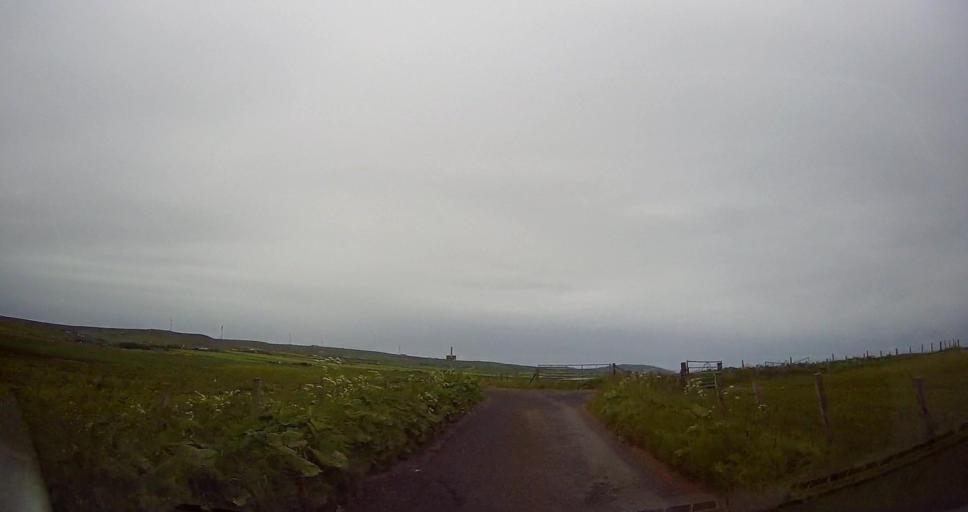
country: GB
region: Scotland
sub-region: Orkney Islands
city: Orkney
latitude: 59.1170
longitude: -3.0830
